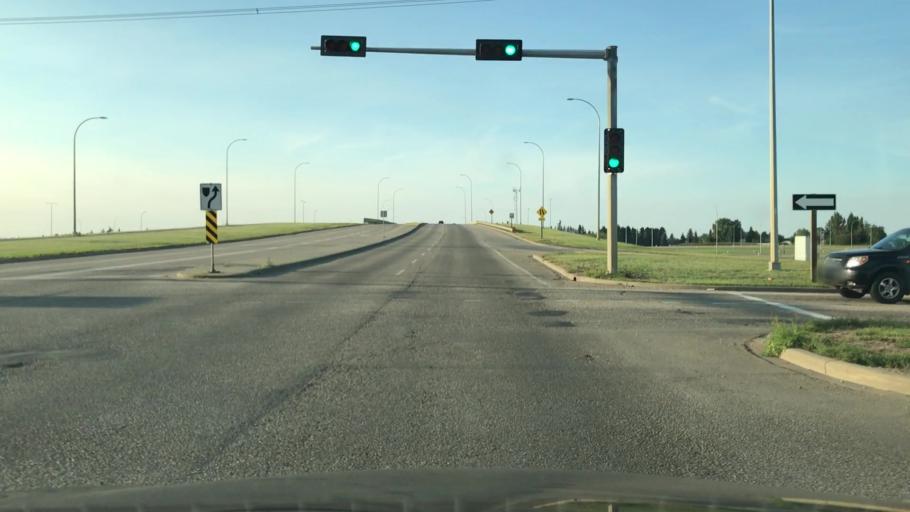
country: CA
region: Alberta
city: Beaumont
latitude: 53.4332
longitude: -113.4178
